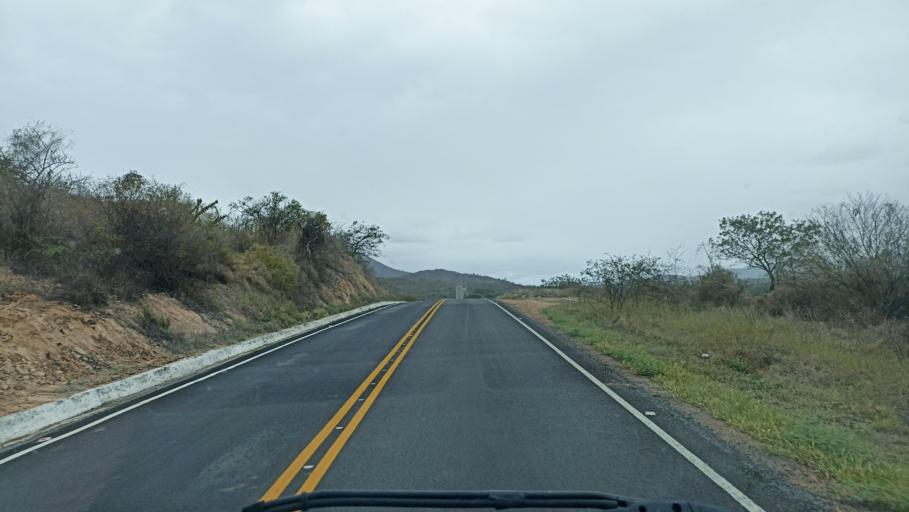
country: BR
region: Bahia
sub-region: Andarai
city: Vera Cruz
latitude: -13.0488
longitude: -40.7565
